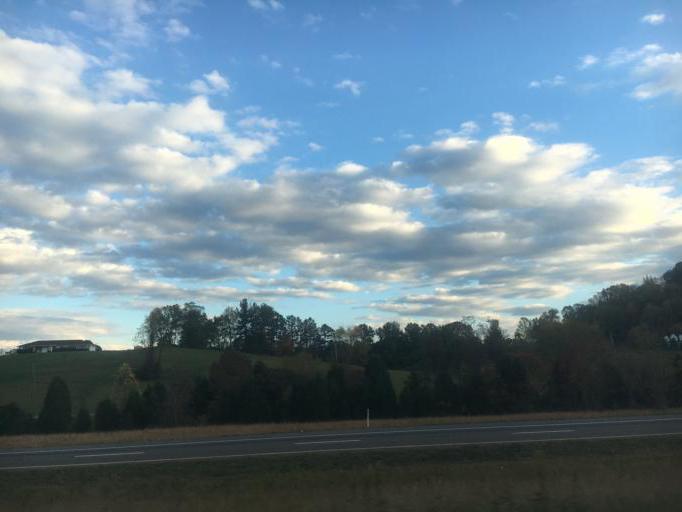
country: US
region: Tennessee
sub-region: Washington County
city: Spurgeon
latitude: 36.5130
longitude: -82.4147
